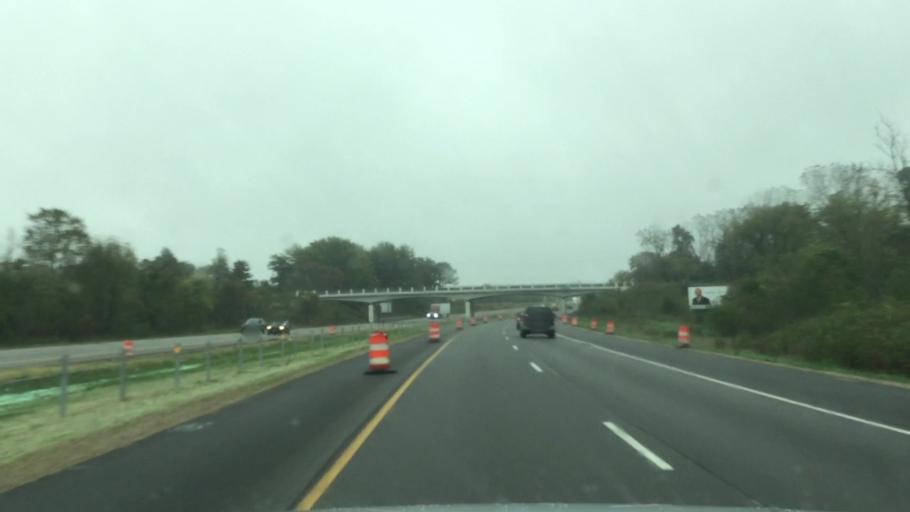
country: US
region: Michigan
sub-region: Van Buren County
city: Decatur
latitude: 42.1962
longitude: -86.0344
